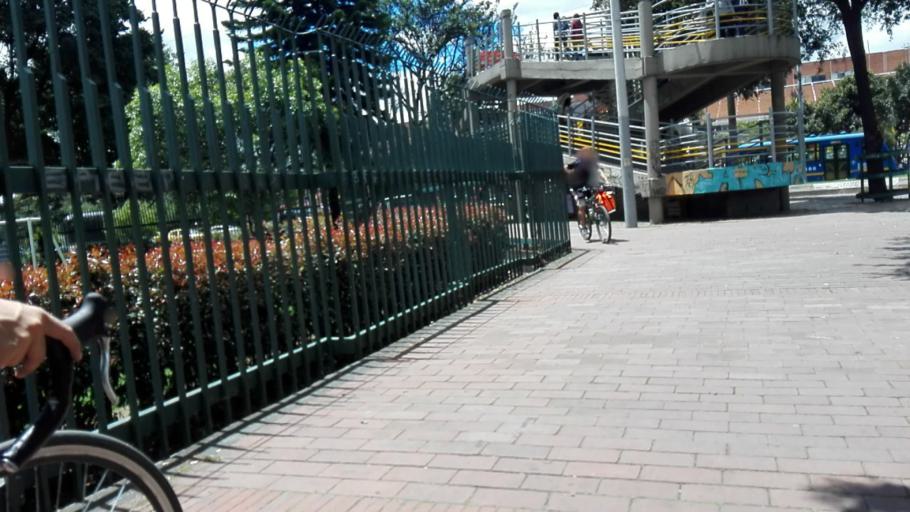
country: CO
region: Bogota D.C.
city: Barrio San Luis
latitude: 4.6826
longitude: -74.0796
